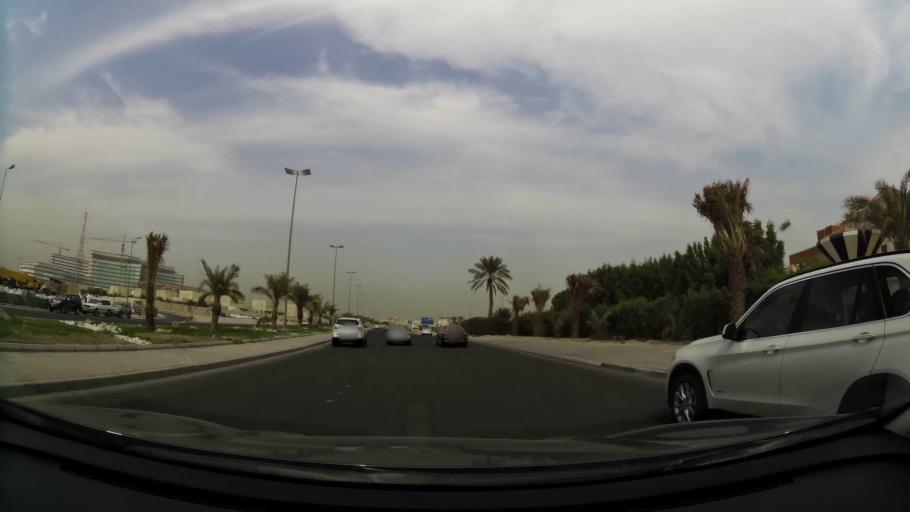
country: KW
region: Mubarak al Kabir
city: Sabah as Salim
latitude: 29.2735
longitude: 48.0223
